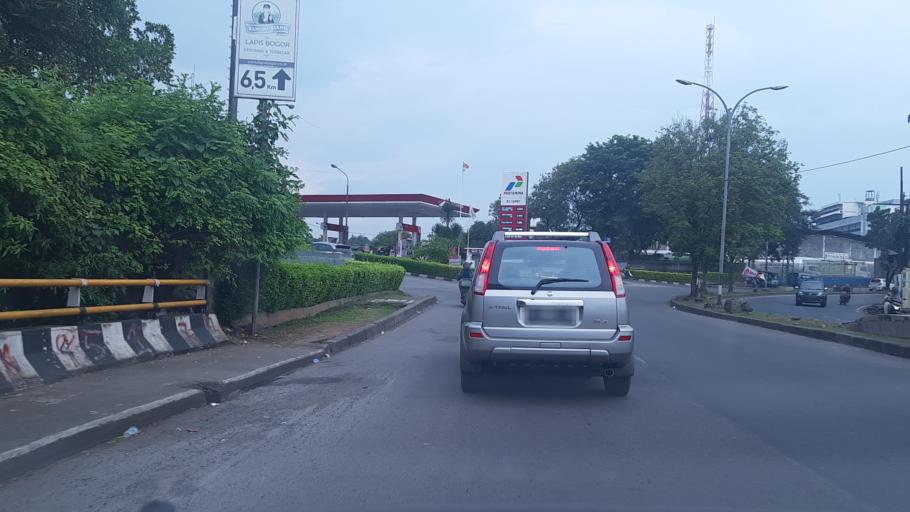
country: ID
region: West Java
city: Cibinong
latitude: -6.4807
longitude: 106.8678
